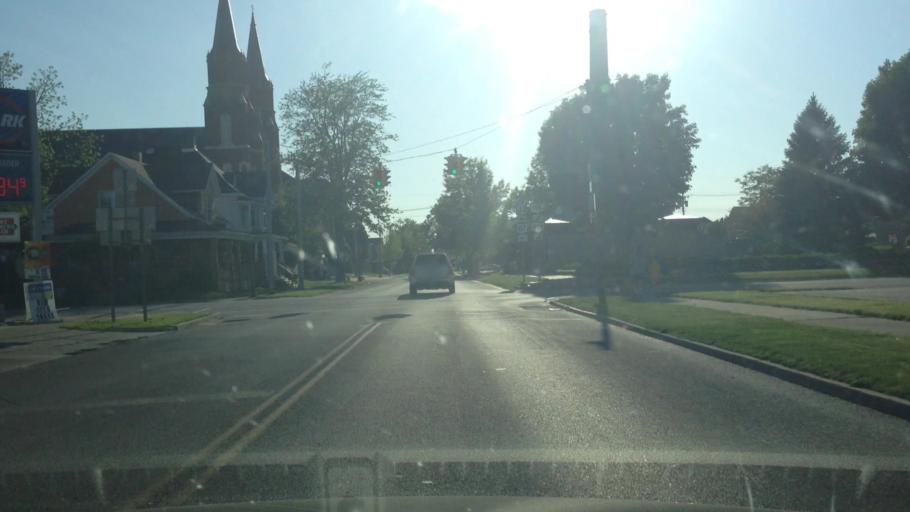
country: US
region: Ohio
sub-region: Auglaize County
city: Wapakoneta
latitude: 40.5679
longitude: -84.1937
